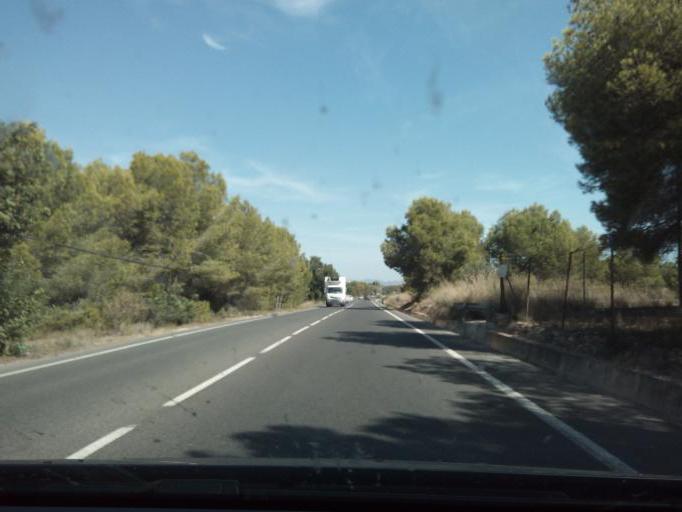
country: ES
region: Valencia
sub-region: Provincia de Valencia
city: Manises
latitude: 39.5361
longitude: -0.4752
